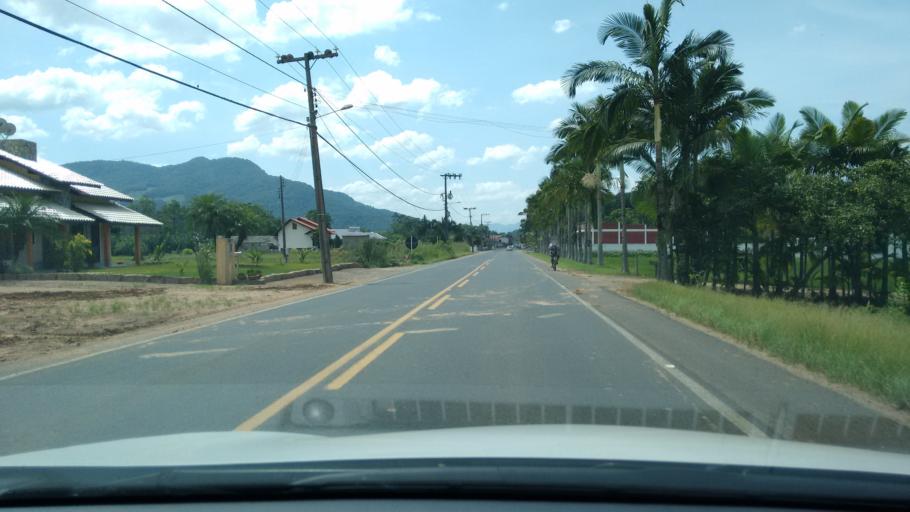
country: BR
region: Santa Catarina
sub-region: Timbo
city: Timbo
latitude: -26.8517
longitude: -49.3300
